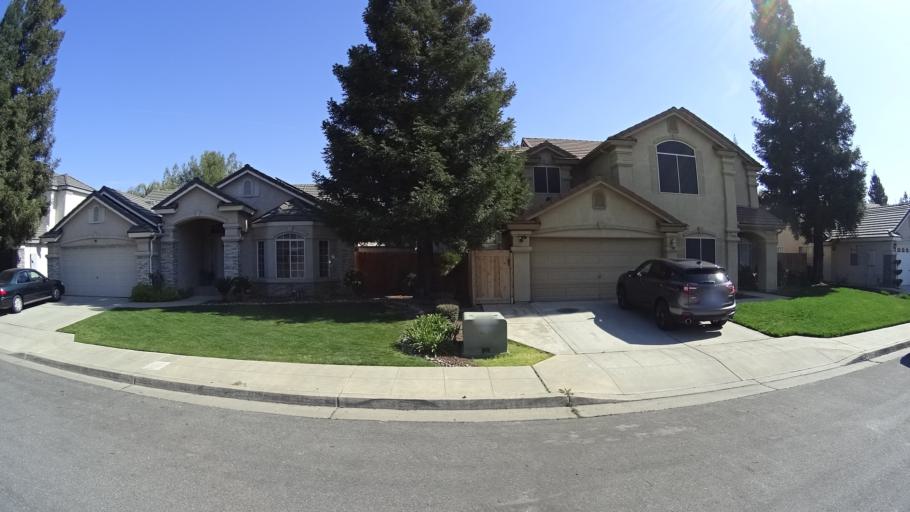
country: US
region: California
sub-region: Fresno County
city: Clovis
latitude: 36.8808
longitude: -119.7407
